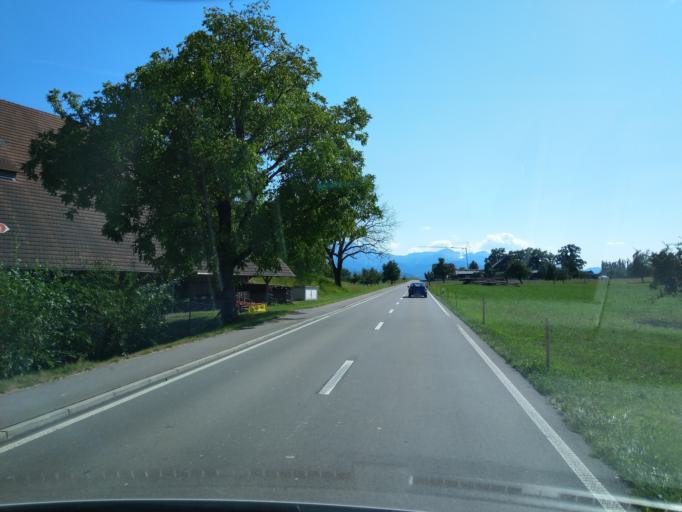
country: CH
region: Lucerne
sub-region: Hochdorf District
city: Emmen
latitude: 47.1084
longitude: 8.2902
